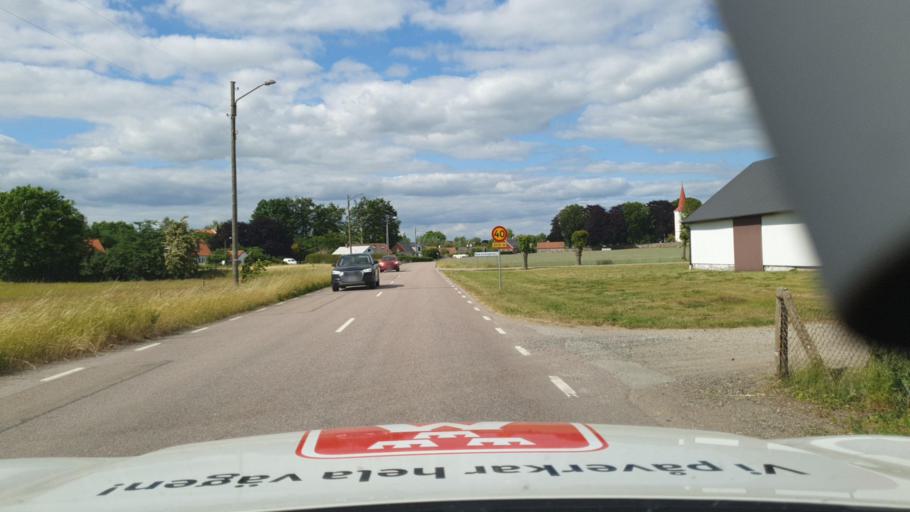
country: SE
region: Skane
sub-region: Ystads Kommun
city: Kopingebro
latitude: 55.4679
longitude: 13.9443
